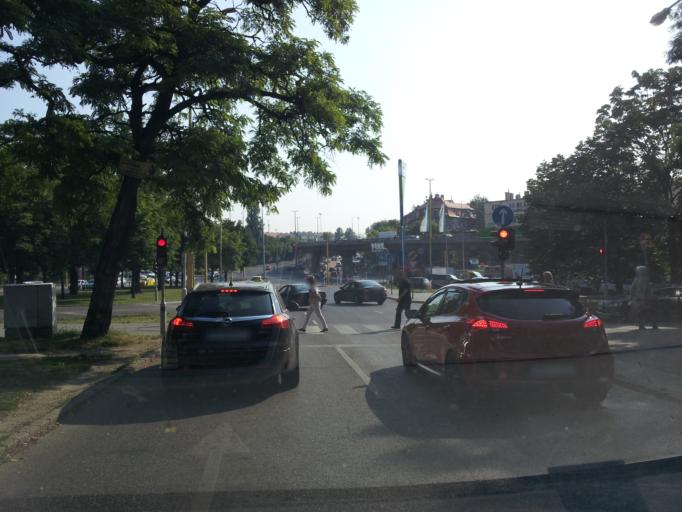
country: HU
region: Budapest
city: Budapest XII. keruelet
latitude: 47.4866
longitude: 19.0232
